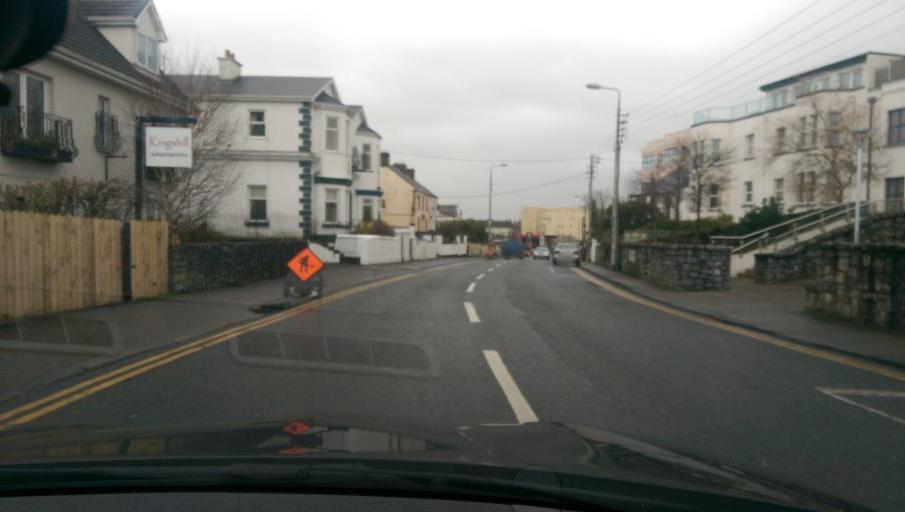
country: IE
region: Connaught
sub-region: County Galway
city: Gaillimh
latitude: 53.2618
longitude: -9.0742
